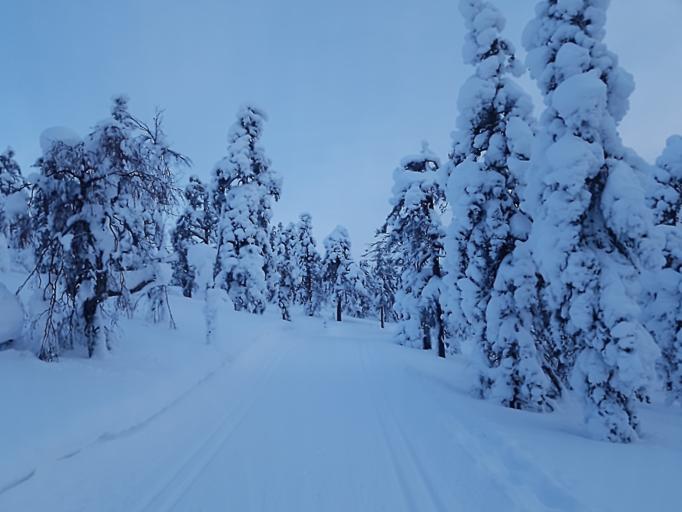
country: FI
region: Lapland
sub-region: Tunturi-Lappi
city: Kolari
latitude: 67.6566
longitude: 24.2427
